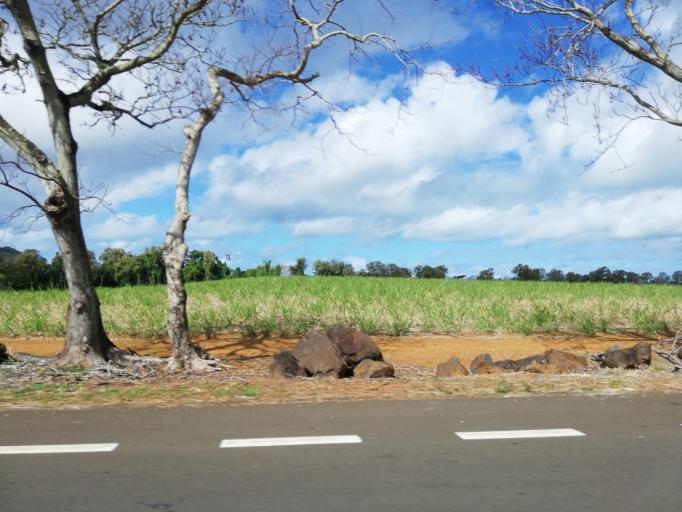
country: MU
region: Grand Port
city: Mahebourg
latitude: -20.3759
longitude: 57.6994
